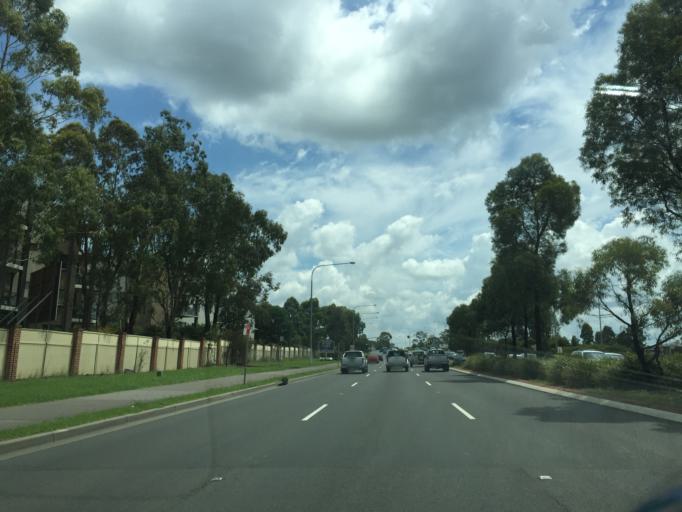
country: AU
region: New South Wales
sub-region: The Hills Shire
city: Beaumont Hills
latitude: -33.6993
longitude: 150.9283
